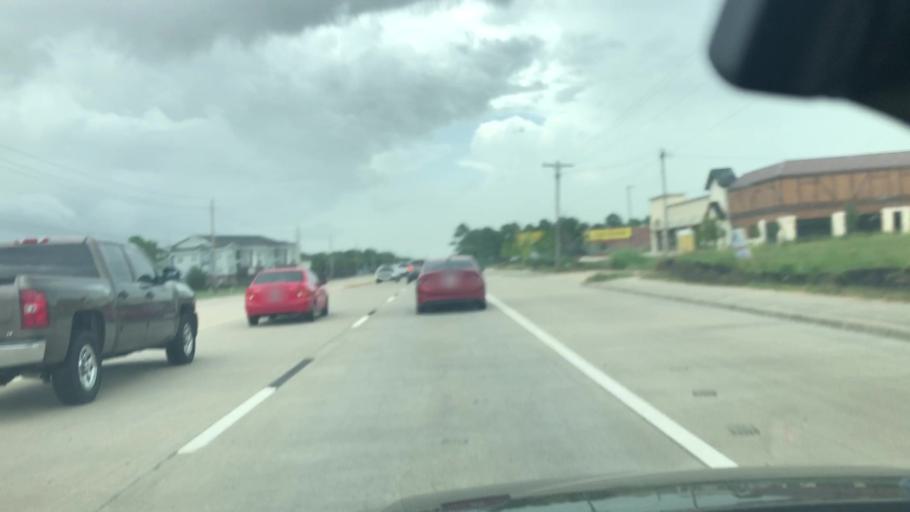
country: US
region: Texas
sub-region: Galveston County
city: Dickinson
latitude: 29.4737
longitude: -95.0793
